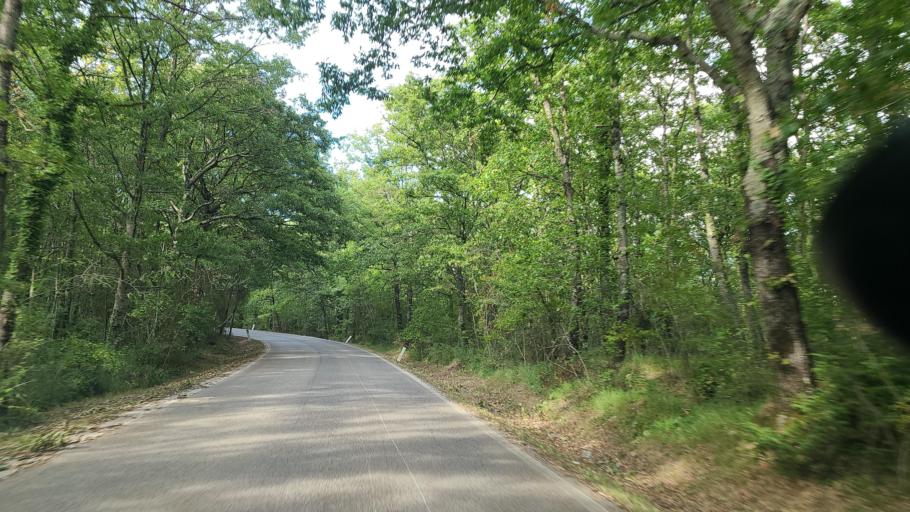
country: IT
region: Tuscany
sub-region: Provincia di Siena
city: San Gimignano
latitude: 43.4315
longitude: 10.9684
